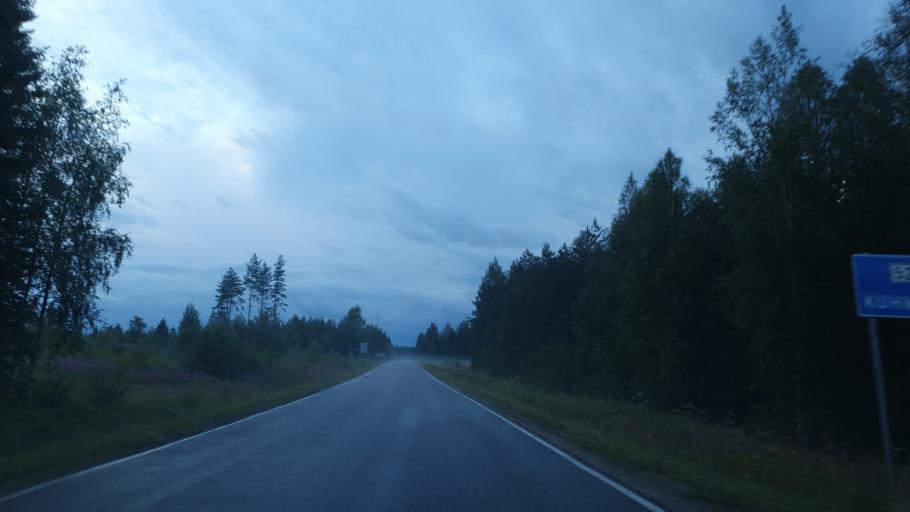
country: FI
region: Kainuu
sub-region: Kehys-Kainuu
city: Kuhmo
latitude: 63.9544
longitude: 29.7179
